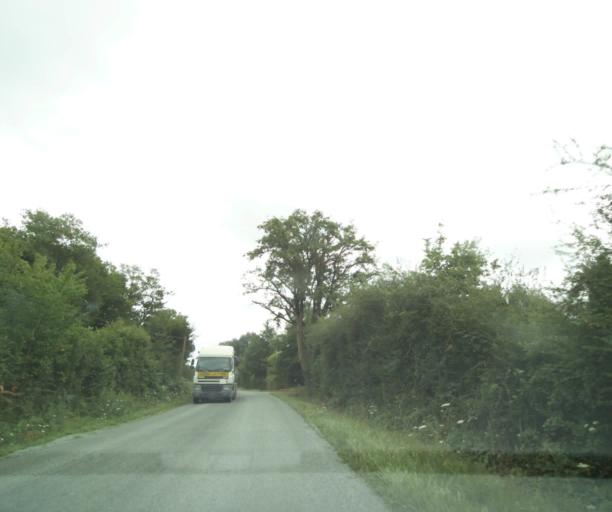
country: FR
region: Pays de la Loire
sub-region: Departement de Maine-et-Loire
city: Durtal
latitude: 47.6922
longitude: -0.2620
